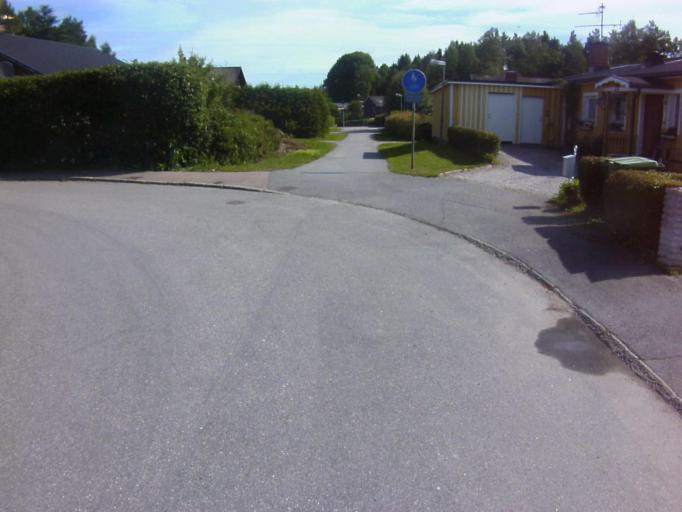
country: SE
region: Soedermanland
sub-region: Eskilstuna Kommun
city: Skogstorp
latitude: 59.3506
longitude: 16.4543
